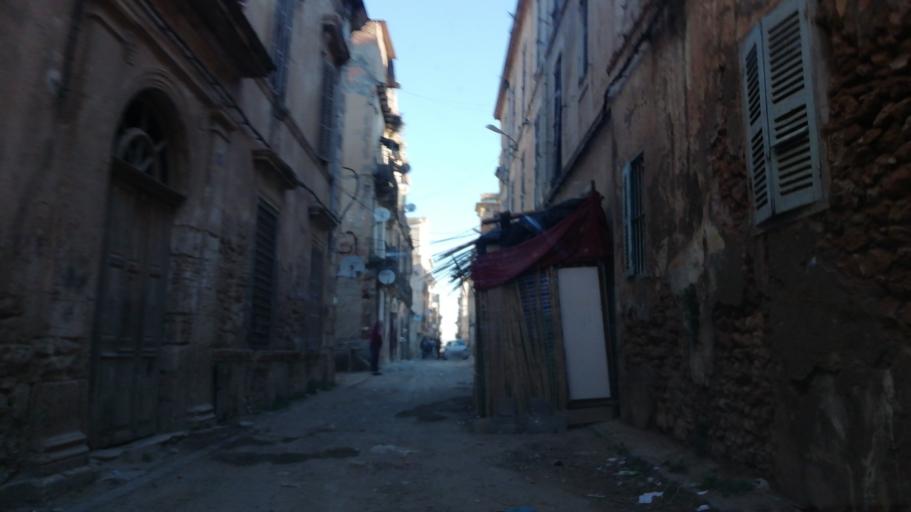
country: DZ
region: Oran
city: Oran
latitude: 35.7009
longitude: -0.6522
